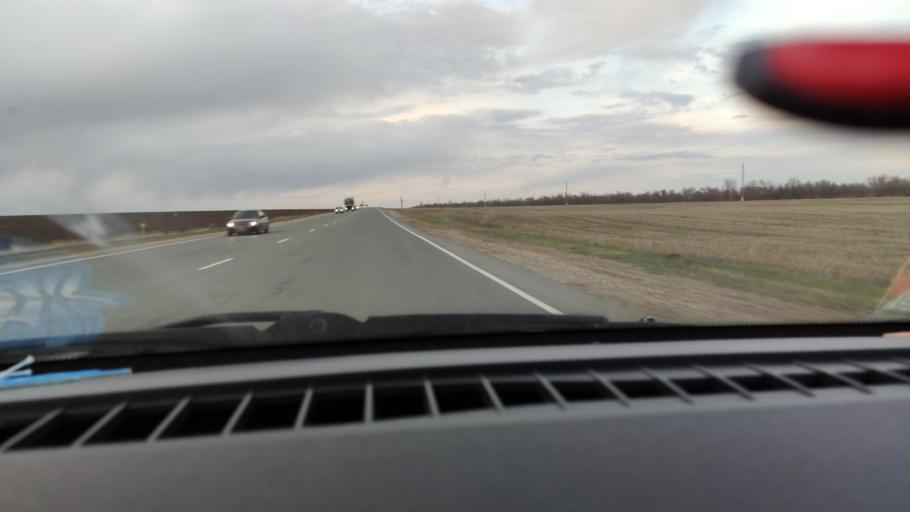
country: RU
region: Saratov
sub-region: Saratovskiy Rayon
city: Saratov
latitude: 51.7432
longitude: 46.0483
